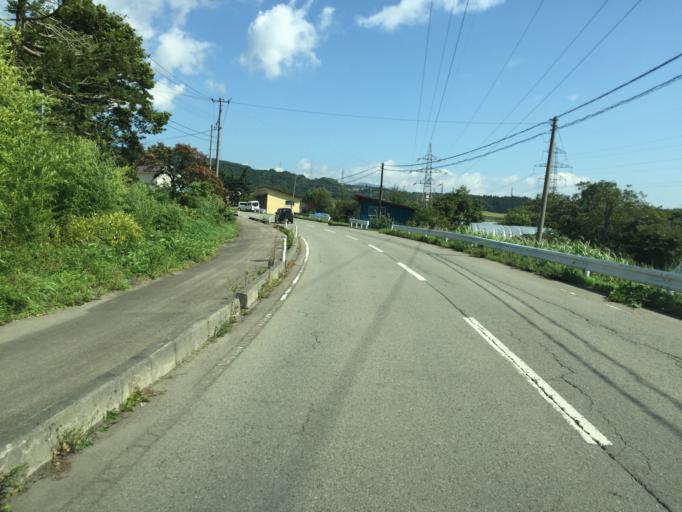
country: JP
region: Fukushima
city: Inawashiro
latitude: 37.5679
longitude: 140.0157
